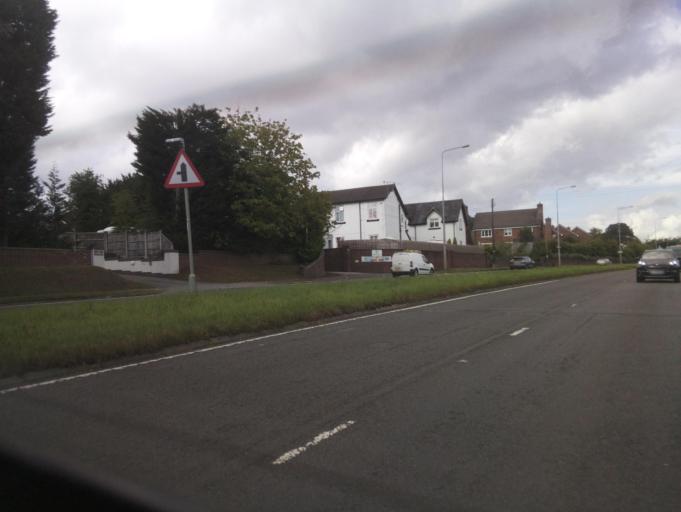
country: GB
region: England
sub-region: Staffordshire
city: Barlaston
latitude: 52.9420
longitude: -2.1888
